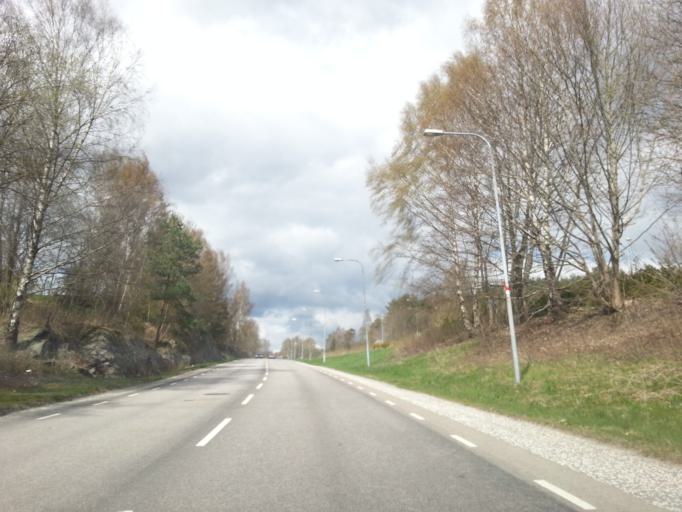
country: SE
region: Vaestra Goetaland
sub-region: Goteborg
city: Hammarkullen
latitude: 57.7737
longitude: 12.0234
